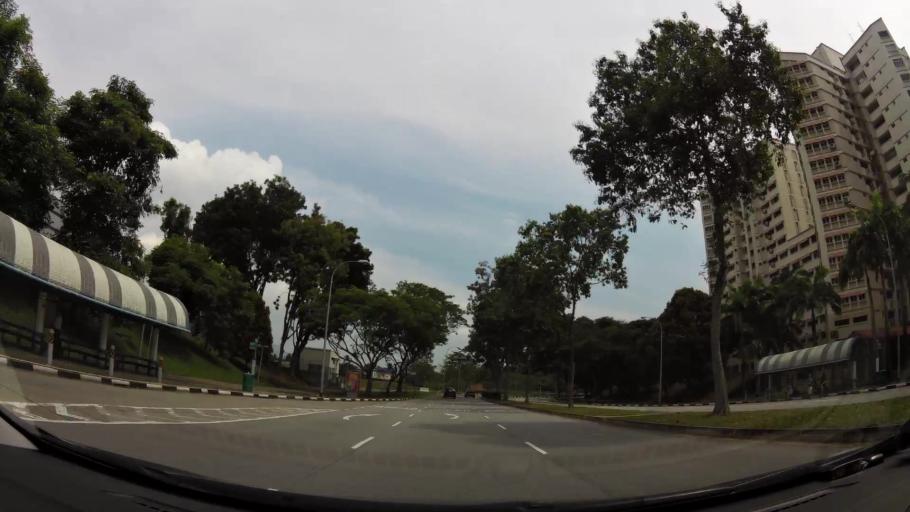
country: MY
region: Johor
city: Kampung Pasir Gudang Baru
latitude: 1.3828
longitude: 103.9359
